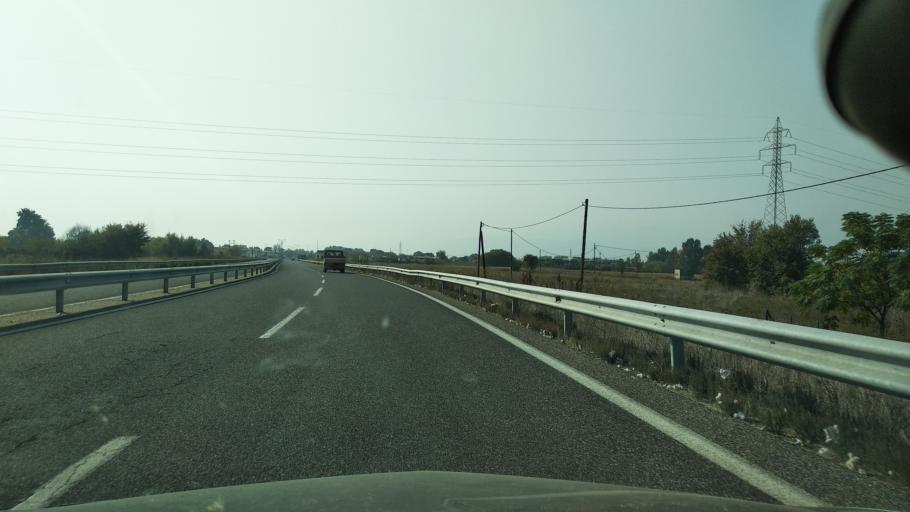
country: GR
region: Thessaly
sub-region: Trikala
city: Trikala
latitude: 39.5622
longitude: 21.8021
